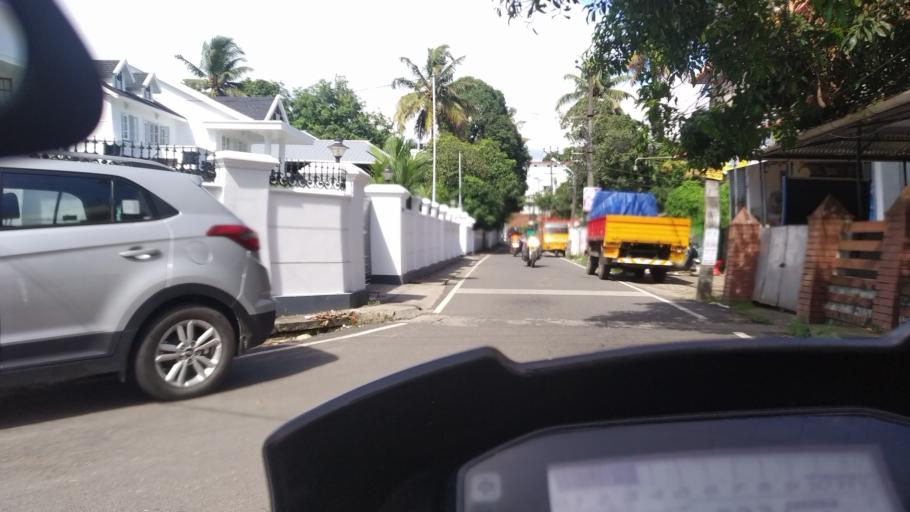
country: IN
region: Kerala
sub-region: Ernakulam
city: Elur
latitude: 10.0226
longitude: 76.2729
